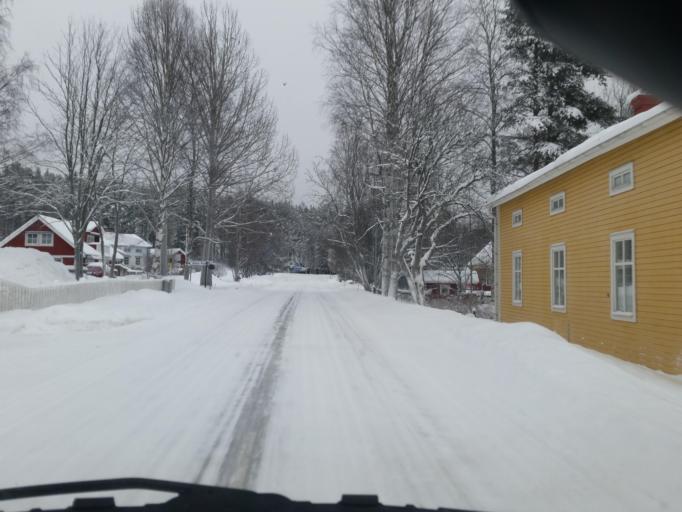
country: SE
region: Norrbotten
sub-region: Pitea Kommun
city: Bergsviken
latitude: 65.3850
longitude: 21.3230
